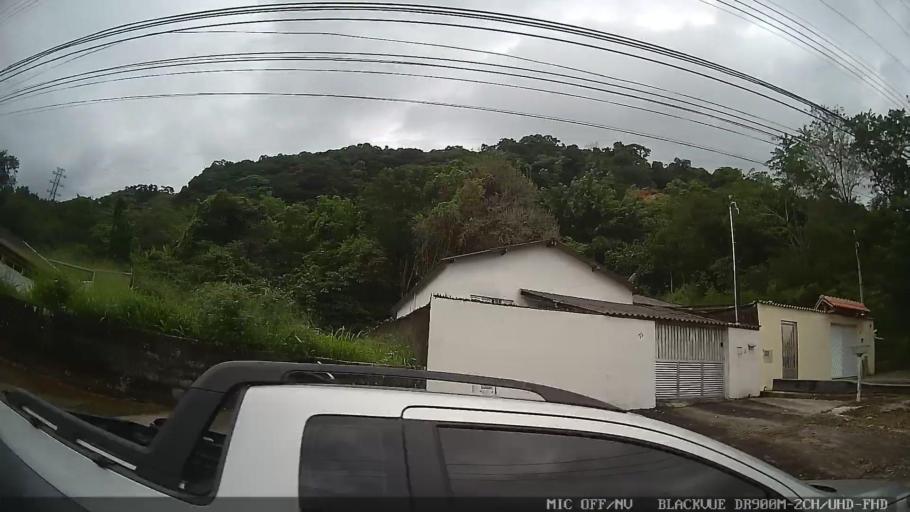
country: BR
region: Sao Paulo
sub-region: Guaruja
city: Guaruja
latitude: -23.9953
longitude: -46.2701
